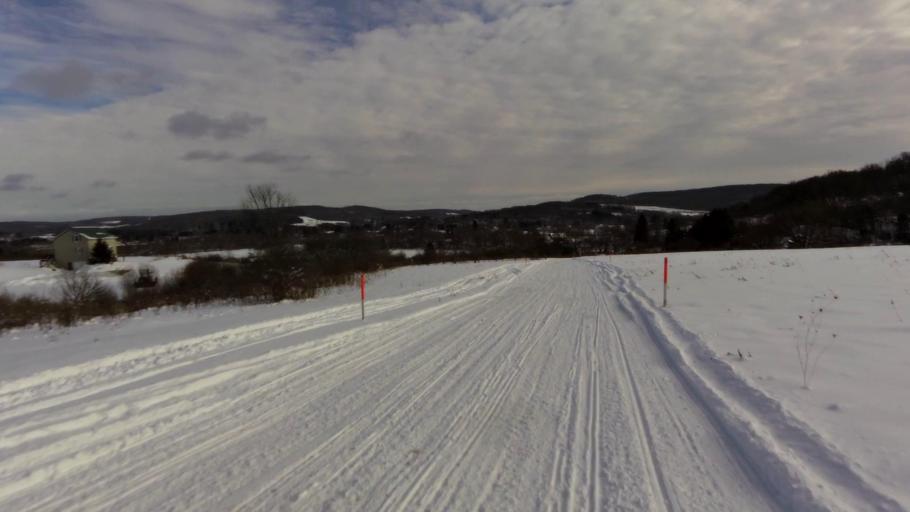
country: US
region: New York
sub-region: Cattaraugus County
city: Franklinville
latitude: 42.3402
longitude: -78.4752
